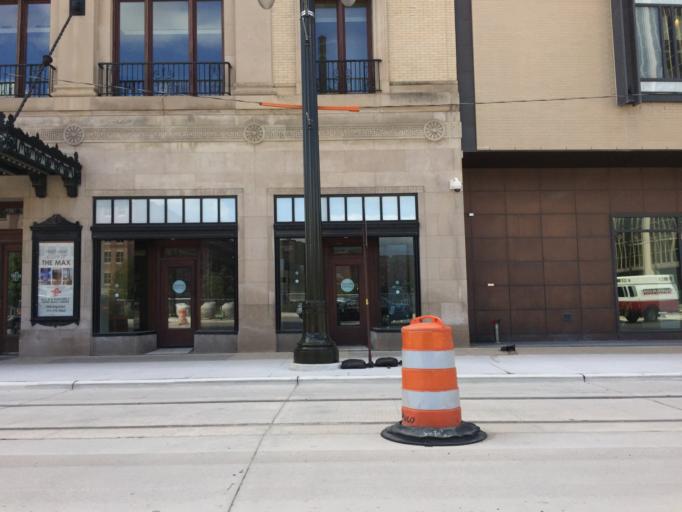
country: US
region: Michigan
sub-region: Wayne County
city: Detroit
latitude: 42.3489
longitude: -83.0590
